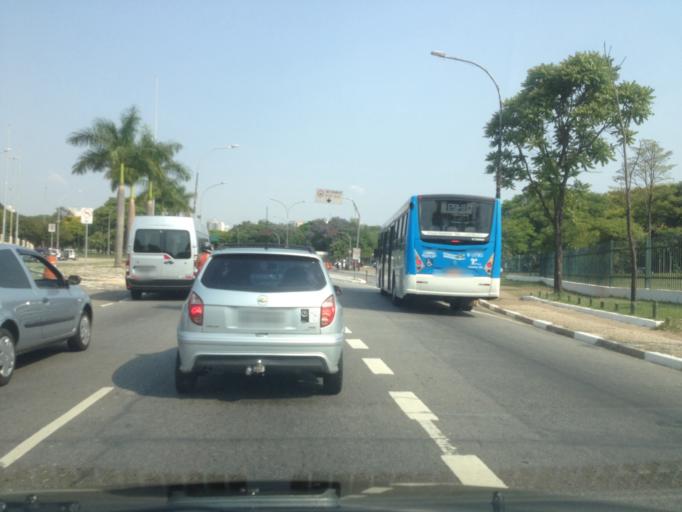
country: BR
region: Sao Paulo
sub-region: Sao Paulo
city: Sao Paulo
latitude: -23.5848
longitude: -46.6560
